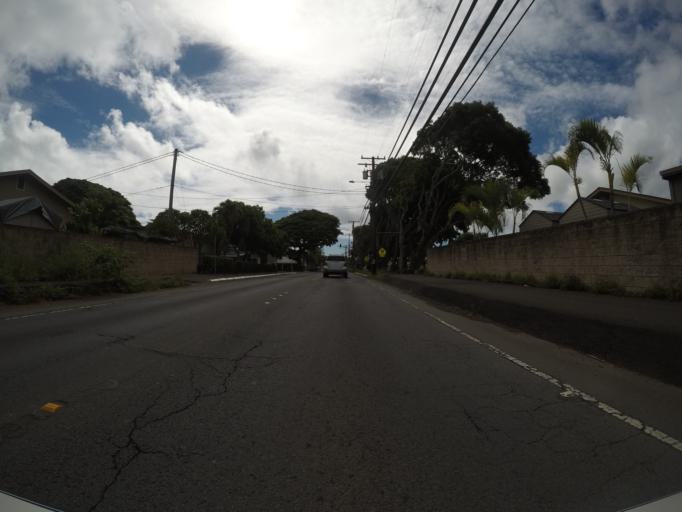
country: US
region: Hawaii
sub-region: Honolulu County
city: Waimanalo
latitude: 21.3472
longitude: -157.7167
